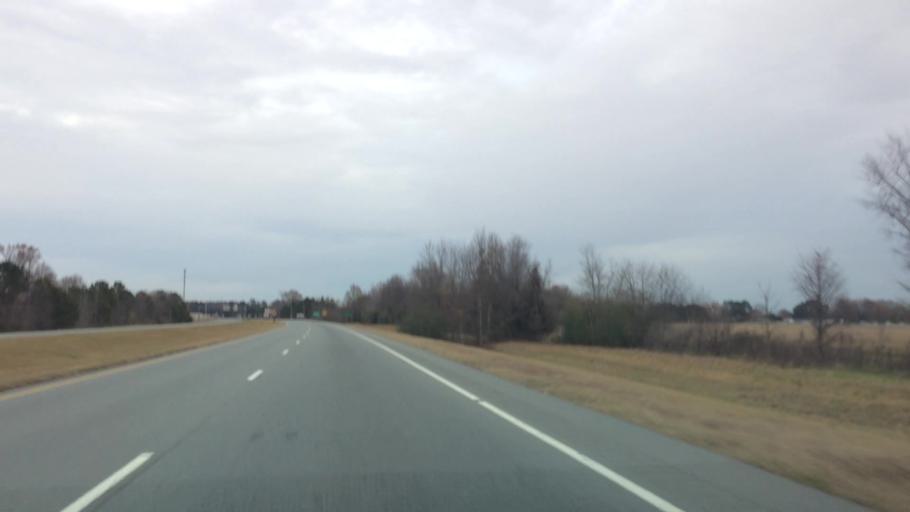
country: US
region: North Carolina
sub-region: Wayne County
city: Mount Olive
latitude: 35.1543
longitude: -78.1145
